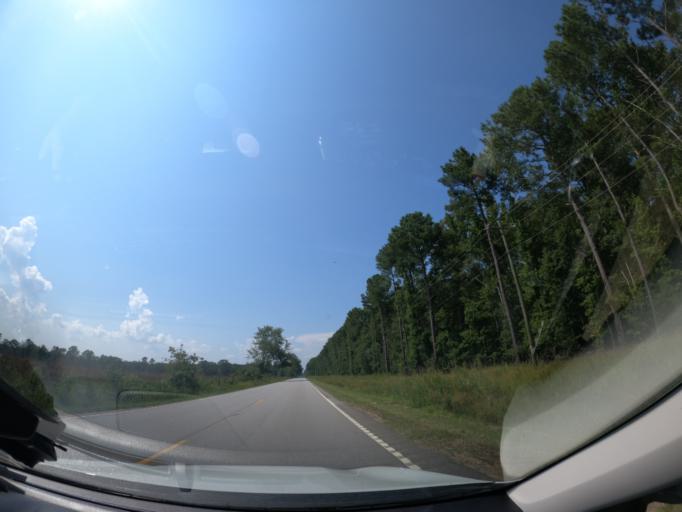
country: US
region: South Carolina
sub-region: Richland County
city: Hopkins
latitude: 33.8799
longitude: -80.9032
